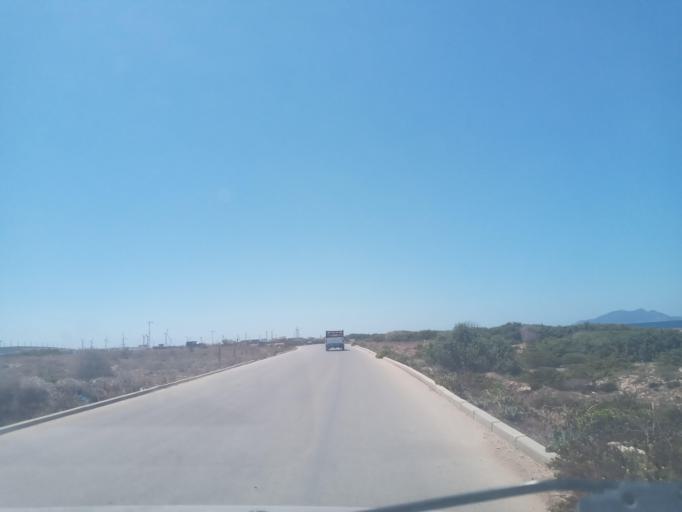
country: TN
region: Nabul
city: El Haouaria
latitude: 37.0498
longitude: 10.9767
